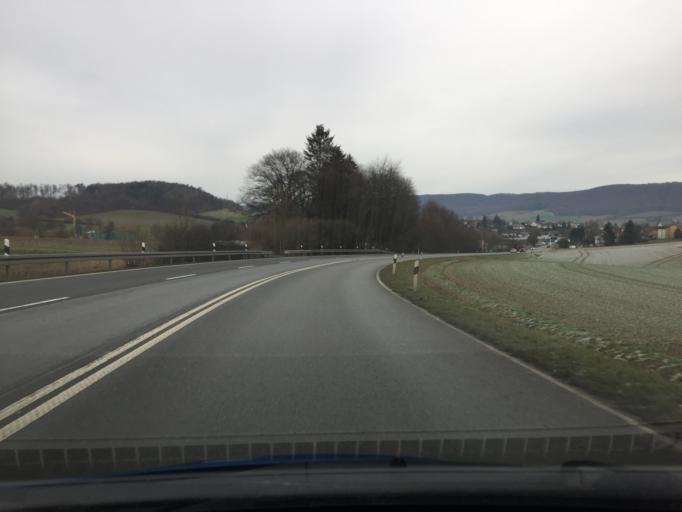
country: DE
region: Lower Saxony
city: Eschershausen
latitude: 51.9235
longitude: 9.6216
